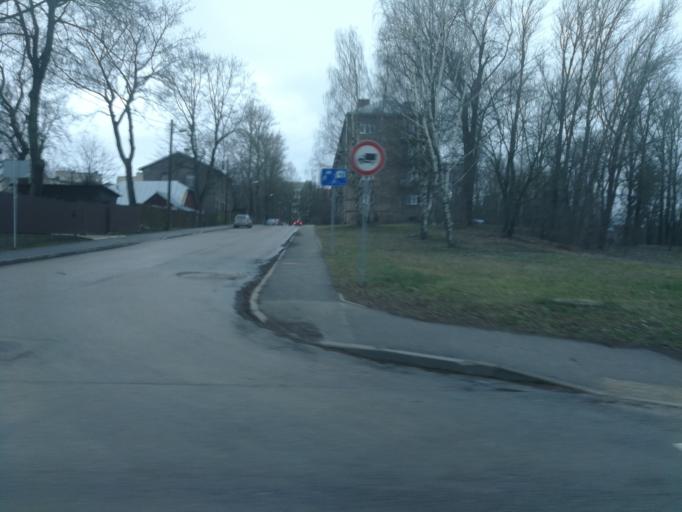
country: LV
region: Riga
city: Jaunciems
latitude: 57.0319
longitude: 24.1155
